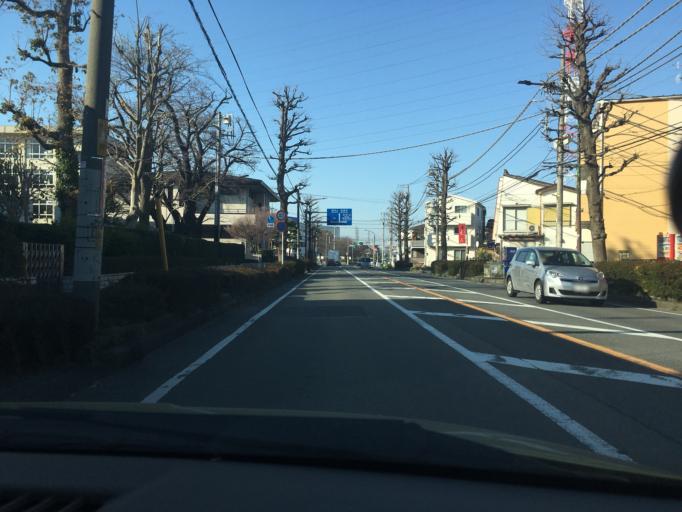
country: JP
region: Tokyo
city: Hachioji
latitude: 35.5858
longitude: 139.3553
